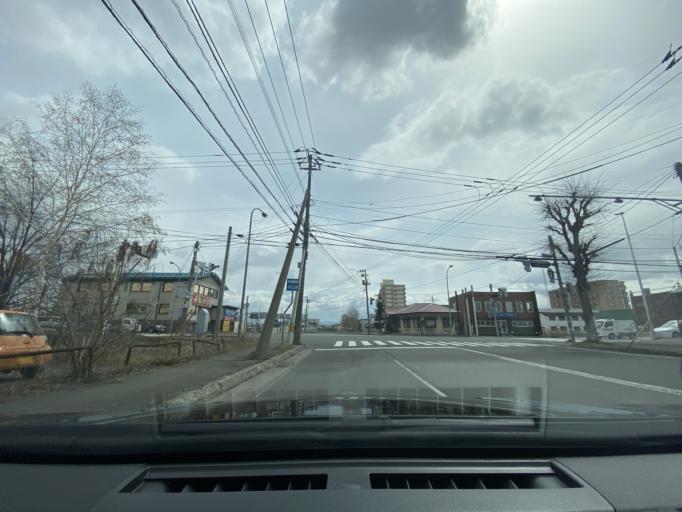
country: JP
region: Hokkaido
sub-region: Asahikawa-shi
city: Asahikawa
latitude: 43.7697
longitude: 142.3803
